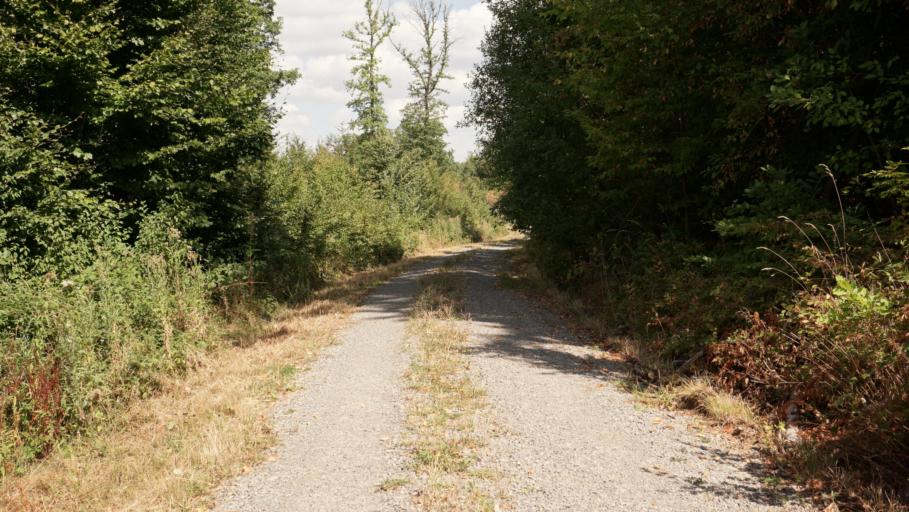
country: DE
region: Baden-Wuerttemberg
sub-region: Karlsruhe Region
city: Mosbach
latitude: 49.3557
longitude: 9.1606
